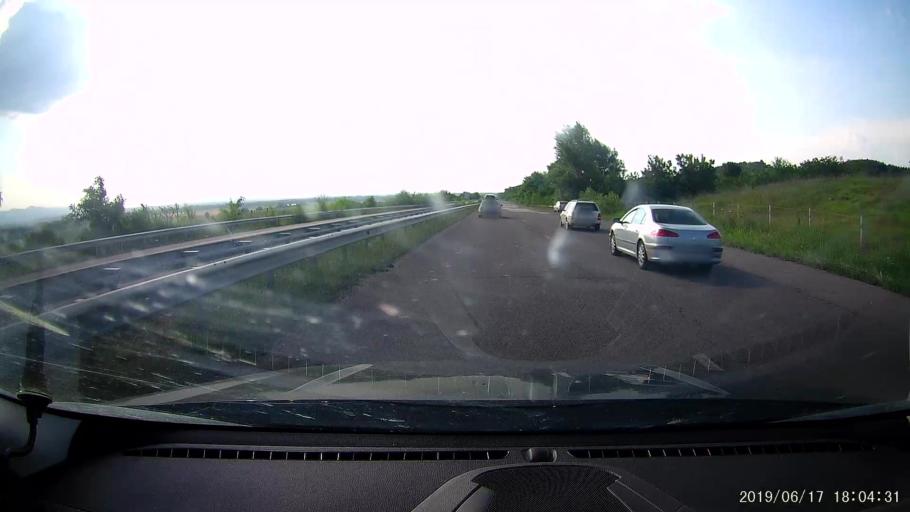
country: BG
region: Khaskovo
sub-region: Obshtina Svilengrad
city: Svilengrad
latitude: 41.7866
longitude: 26.1964
